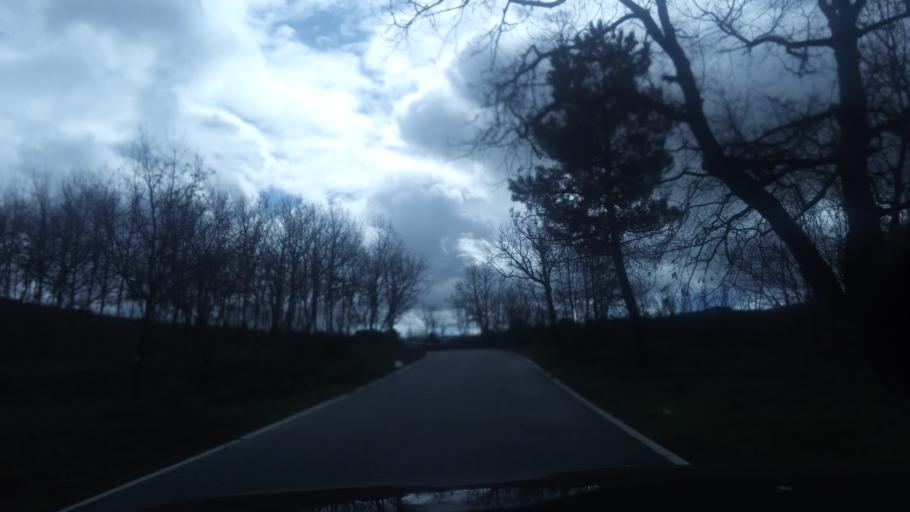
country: PT
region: Guarda
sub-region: Fornos de Algodres
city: Fornos de Algodres
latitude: 40.5856
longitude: -7.4837
